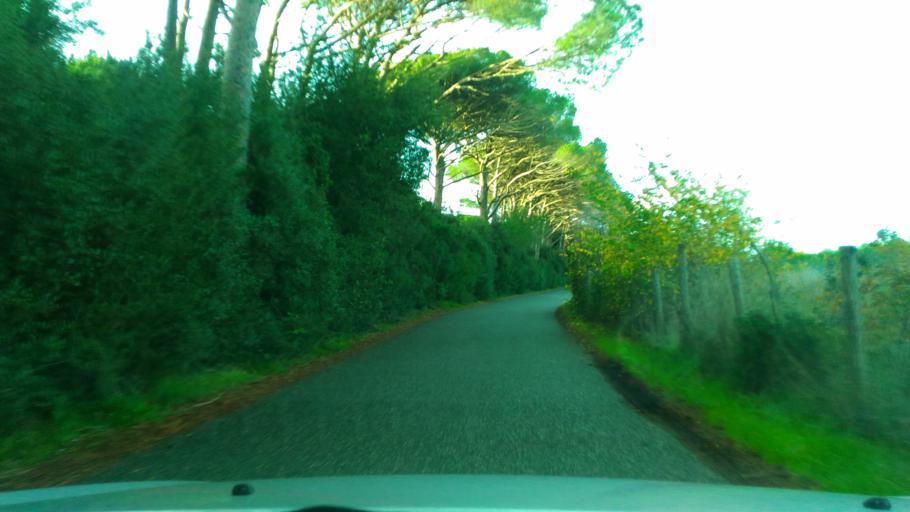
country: IT
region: Tuscany
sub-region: Provincia di Livorno
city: Cecina
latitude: 43.2859
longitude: 10.5107
